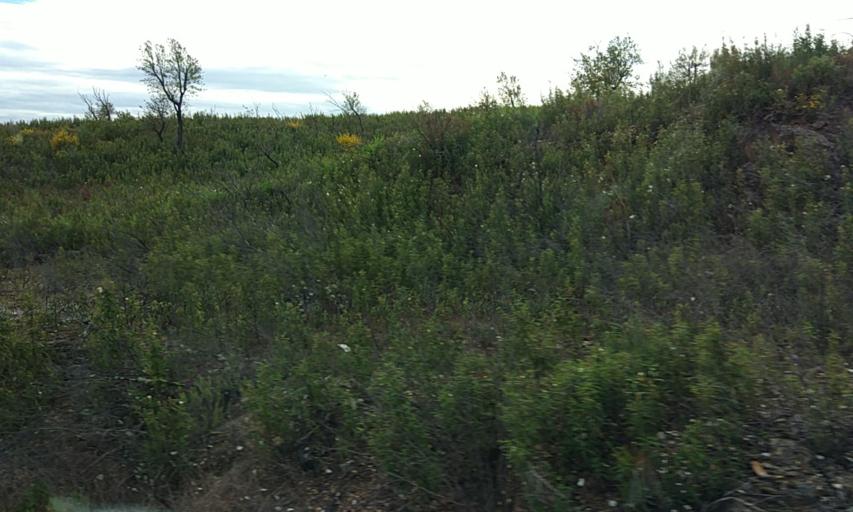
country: ES
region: Extremadura
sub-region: Provincia de Caceres
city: Perales del Puerto
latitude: 40.1760
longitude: -6.6748
